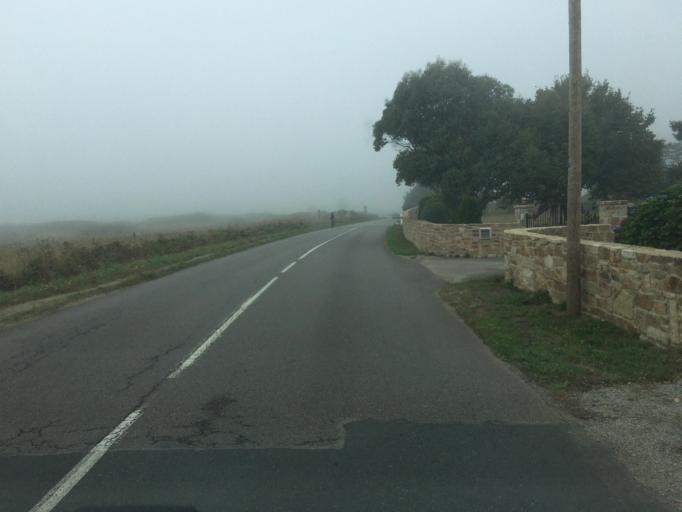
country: FR
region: Brittany
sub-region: Departement du Finistere
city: Plogoff
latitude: 48.0630
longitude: -4.6307
